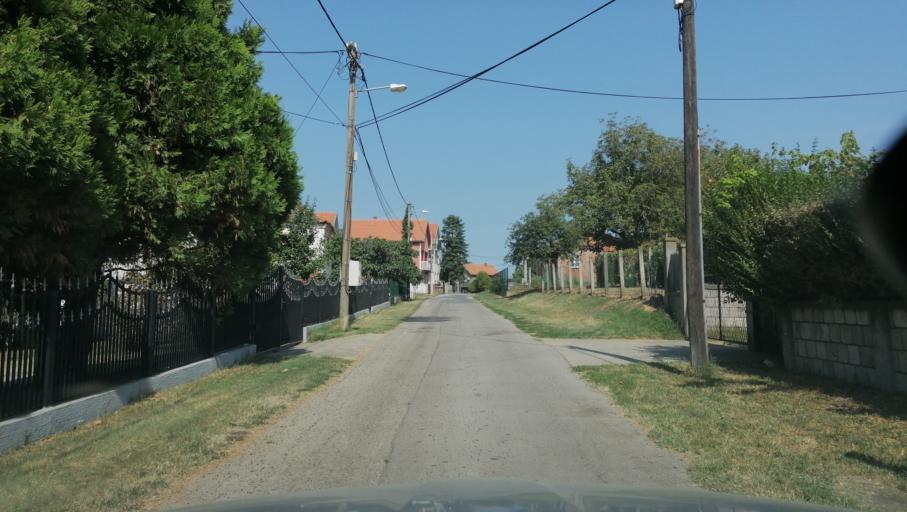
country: RS
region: Central Serbia
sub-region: Belgrade
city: Zvezdara
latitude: 44.6963
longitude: 20.5502
